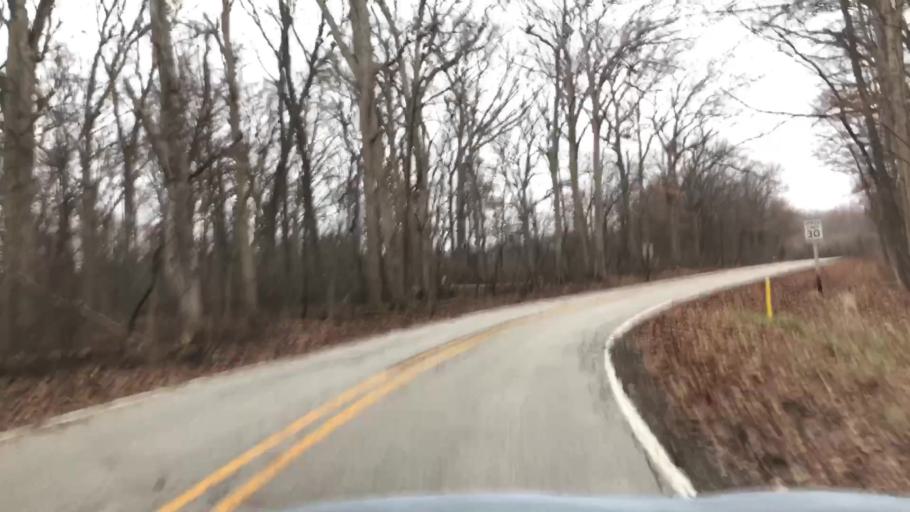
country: US
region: Illinois
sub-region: McLean County
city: Hudson
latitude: 40.6420
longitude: -88.9147
